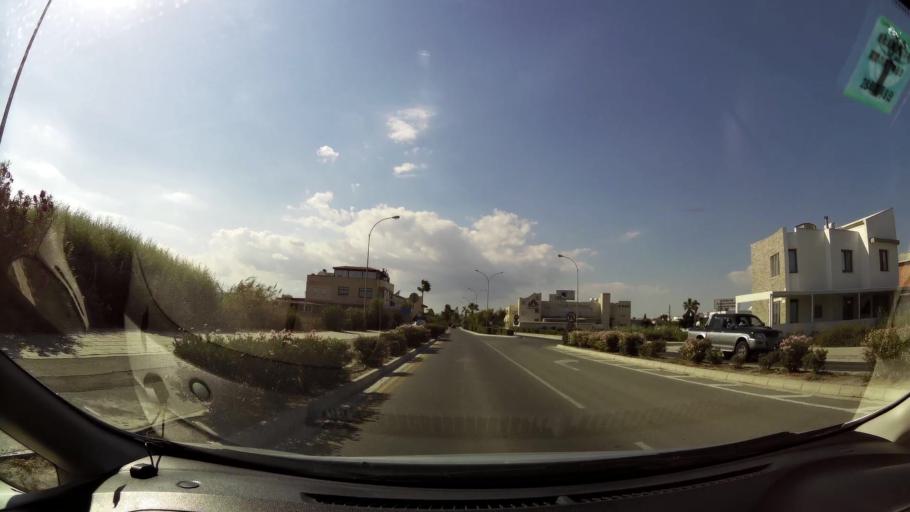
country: CY
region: Larnaka
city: Livadia
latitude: 34.9440
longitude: 33.6370
